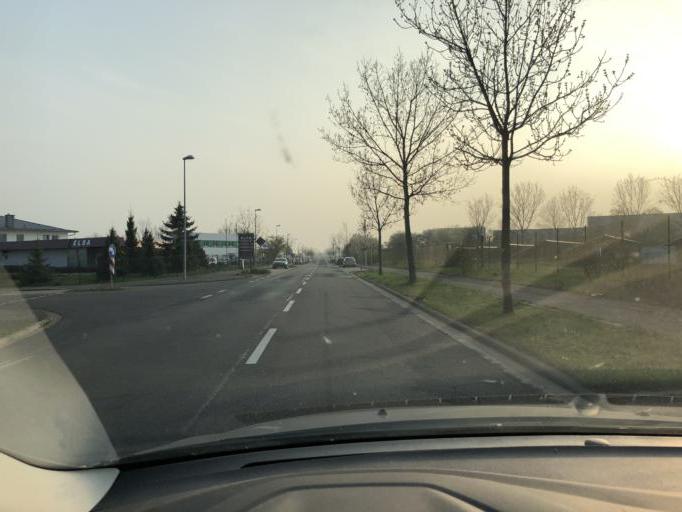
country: DE
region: Saxony
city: Rackwitz
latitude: 51.4057
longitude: 12.3613
